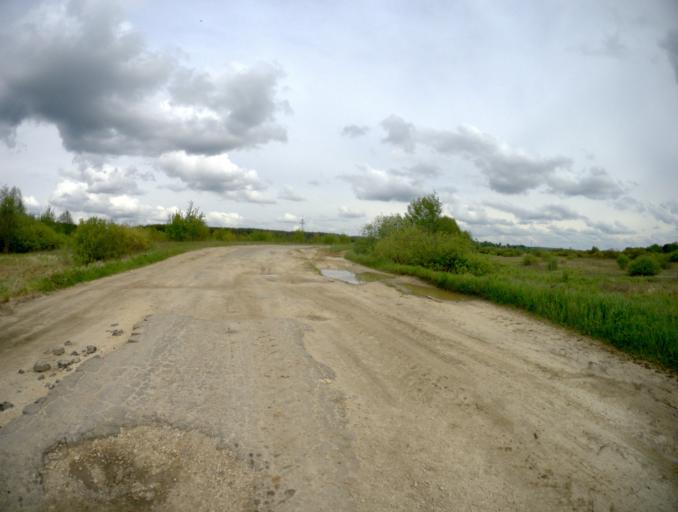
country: RU
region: Rjazan
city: Gus'-Zheleznyy
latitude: 55.0109
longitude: 41.1693
